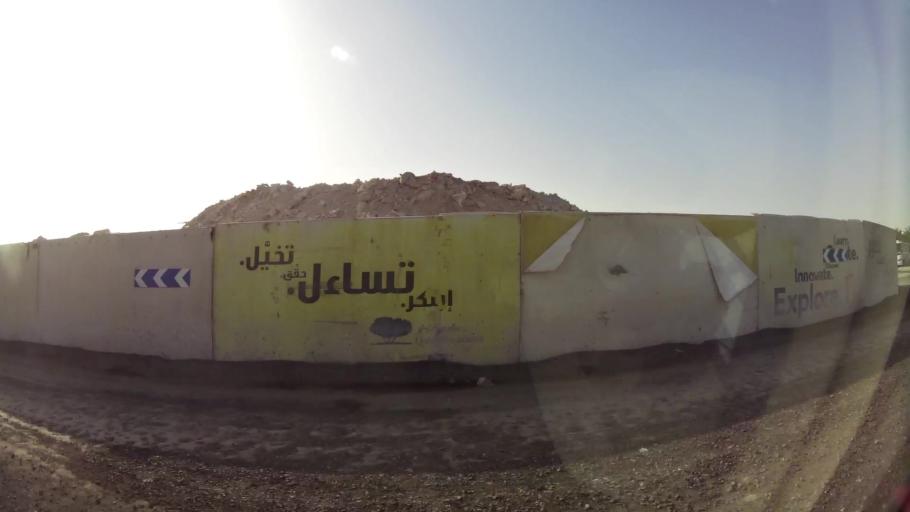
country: QA
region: Baladiyat ar Rayyan
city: Ar Rayyan
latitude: 25.3277
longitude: 51.4298
